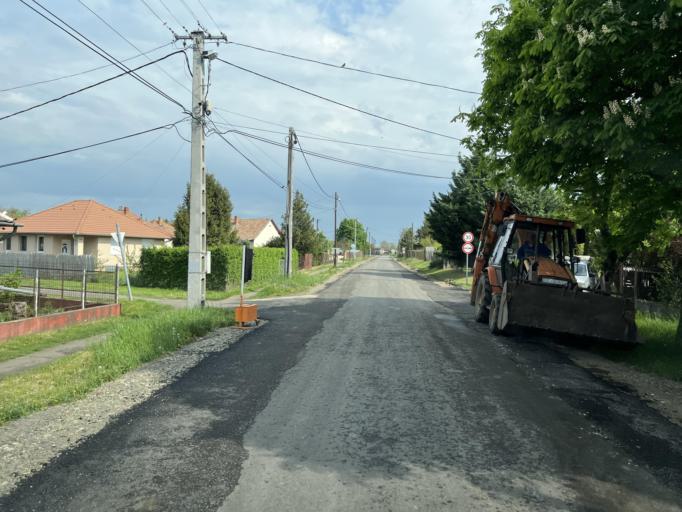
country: HU
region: Pest
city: Tapioszele
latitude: 47.3432
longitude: 19.8741
